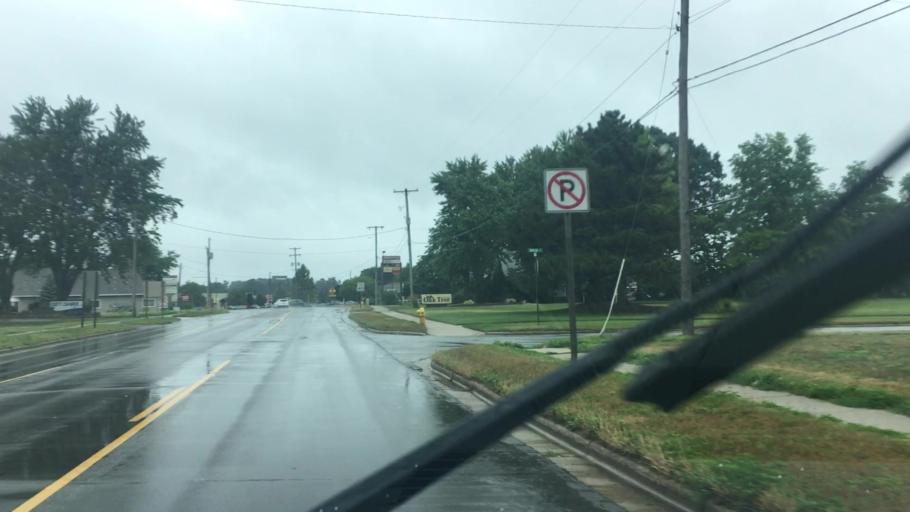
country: US
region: Michigan
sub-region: Ottawa County
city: Hudsonville
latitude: 42.8848
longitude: -85.8526
